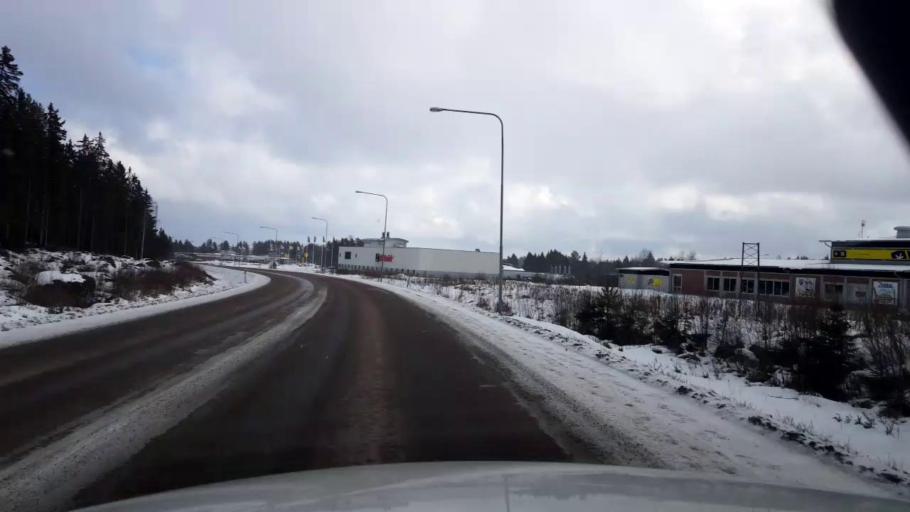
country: SE
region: Gaevleborg
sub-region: Hudiksvalls Kommun
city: Hudiksvall
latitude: 61.7396
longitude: 17.0808
